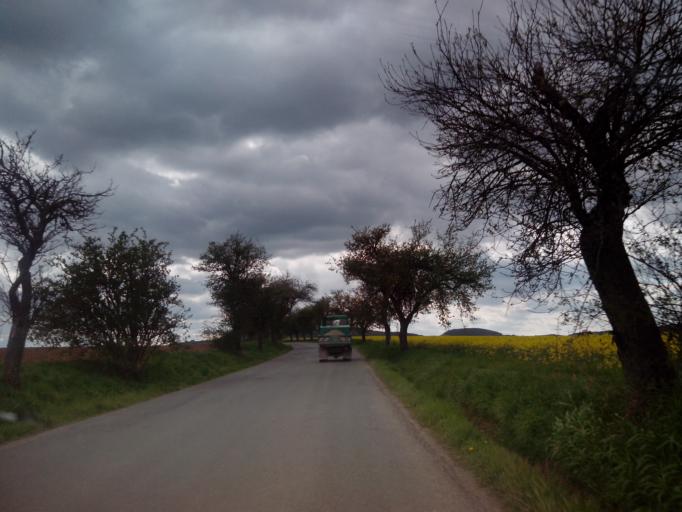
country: CZ
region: Central Bohemia
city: Revnice
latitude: 49.9171
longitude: 14.1584
